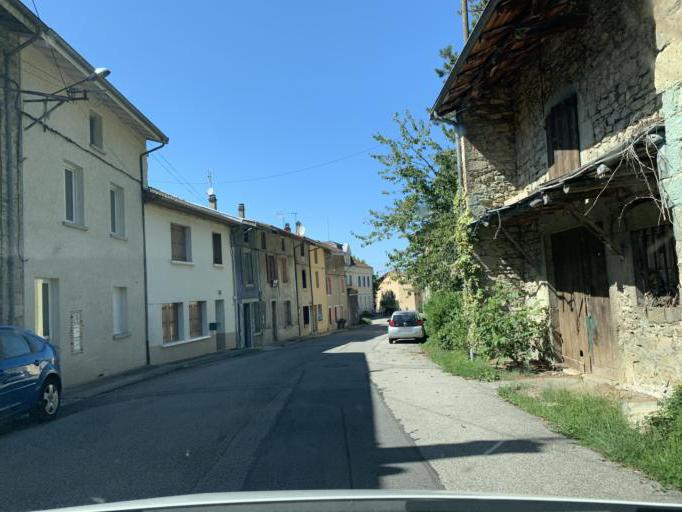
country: FR
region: Rhone-Alpes
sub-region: Departement de l'Ain
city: Saint-Sorlin-en-Bugey
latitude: 45.9204
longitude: 5.3974
